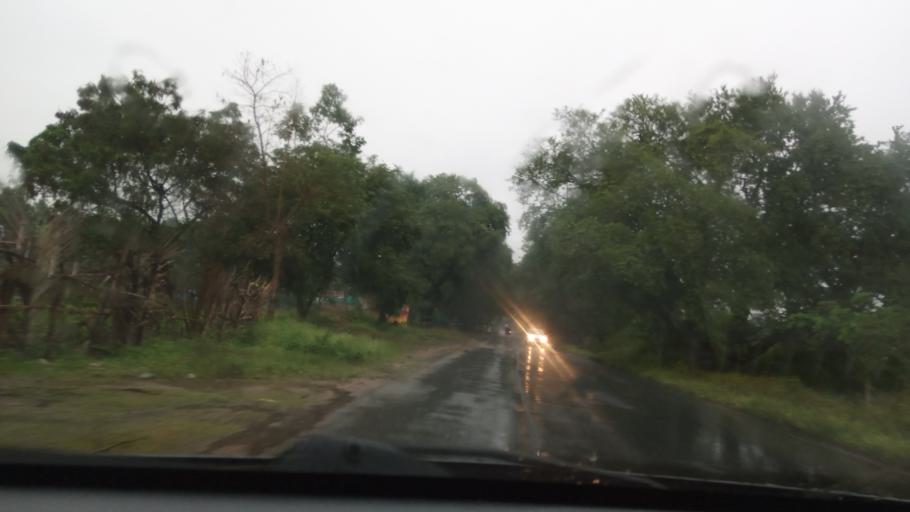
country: IN
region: Tamil Nadu
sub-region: Vellore
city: Walajapet
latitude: 12.8559
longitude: 79.3823
